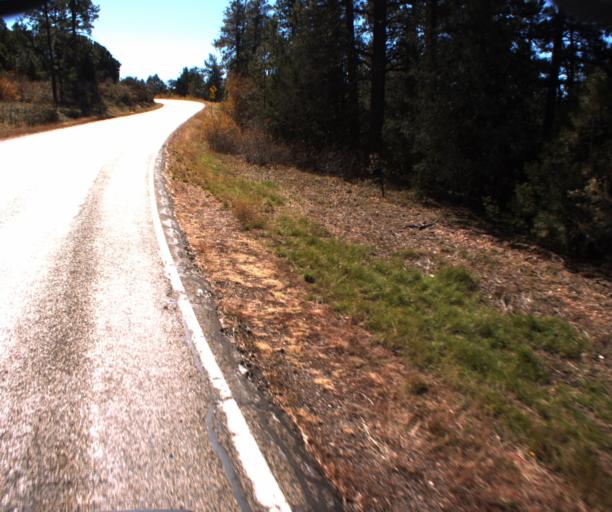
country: US
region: Arizona
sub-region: Coconino County
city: Fredonia
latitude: 36.7770
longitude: -112.2559
